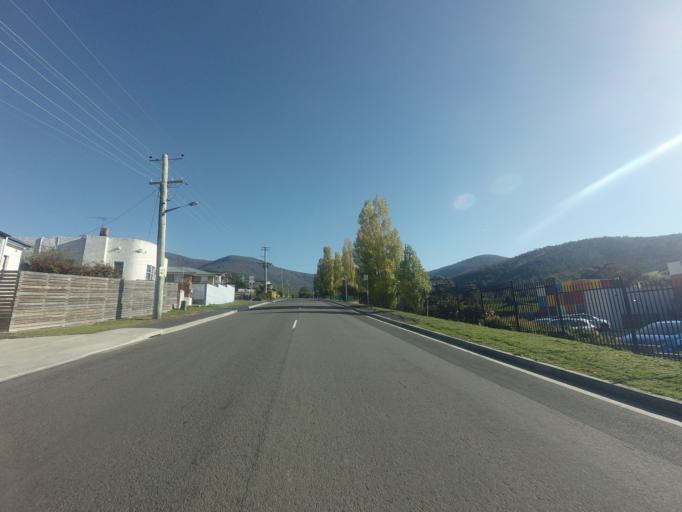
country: AU
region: Tasmania
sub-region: Glenorchy
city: West Moonah
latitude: -42.8496
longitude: 147.2586
